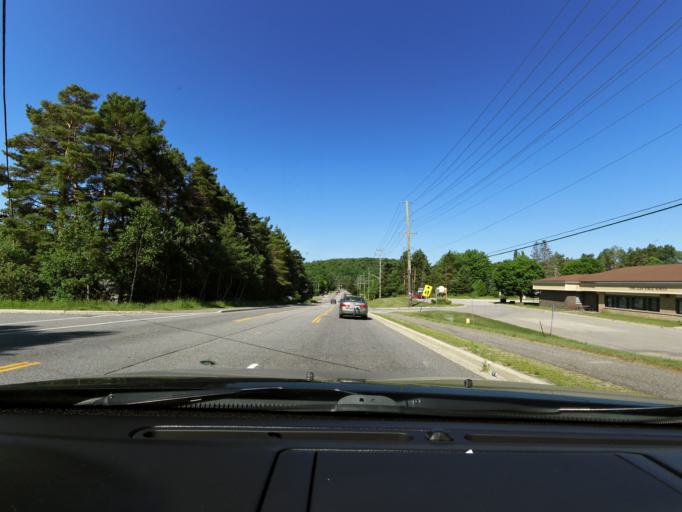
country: CA
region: Ontario
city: Huntsville
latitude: 45.3320
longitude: -79.2287
